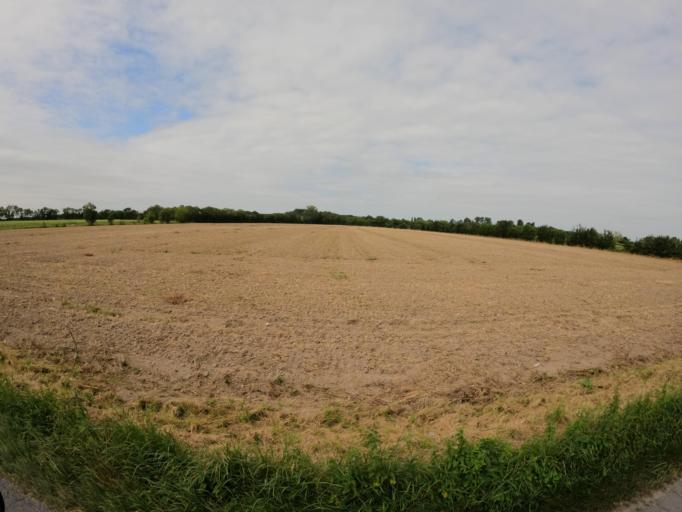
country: FR
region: Poitou-Charentes
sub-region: Departement de la Charente-Maritime
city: Saint-Jean-de-Liversay
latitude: 46.2626
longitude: -0.8810
